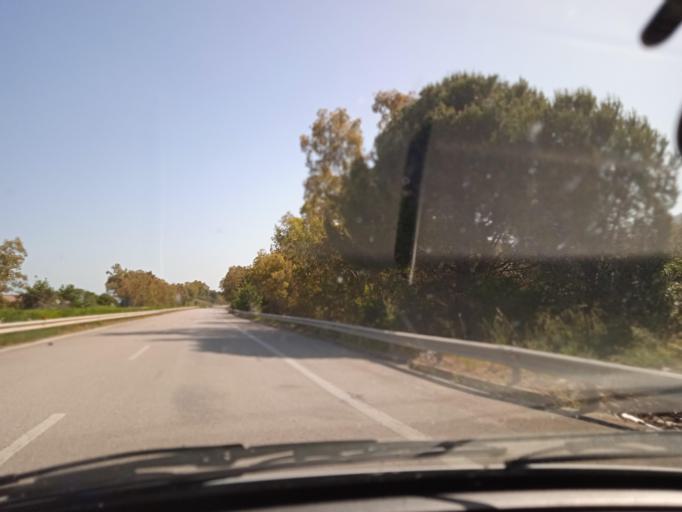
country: IT
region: Sicily
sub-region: Messina
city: Sant'Agata di Militello
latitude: 38.0702
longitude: 14.6544
